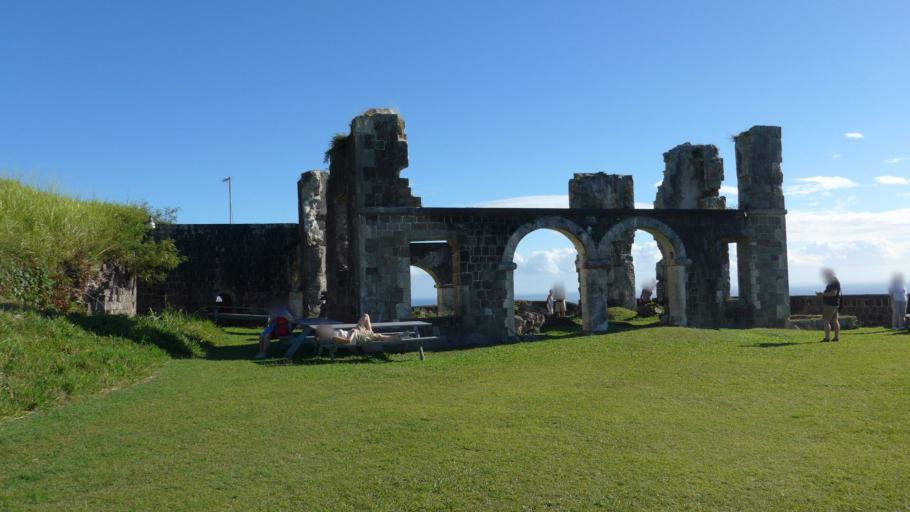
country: KN
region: Saint Anne Sandy Point
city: Sandy Point Town
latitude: 17.3464
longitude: -62.8355
